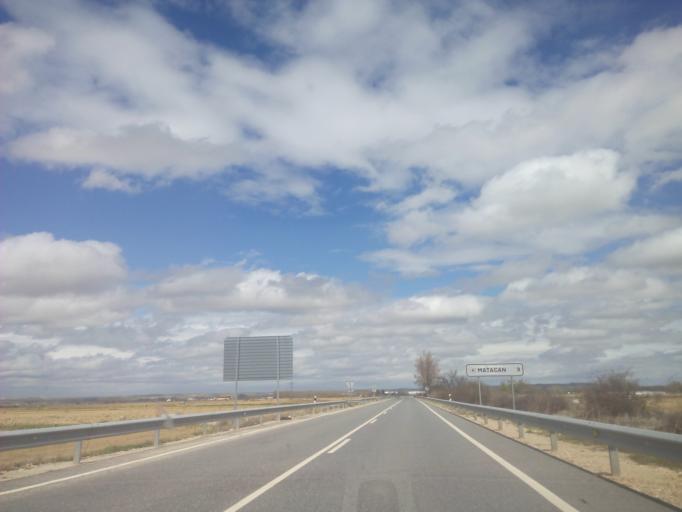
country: ES
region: Castille and Leon
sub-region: Provincia de Salamanca
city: Machacon
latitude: 40.9242
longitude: -5.5053
